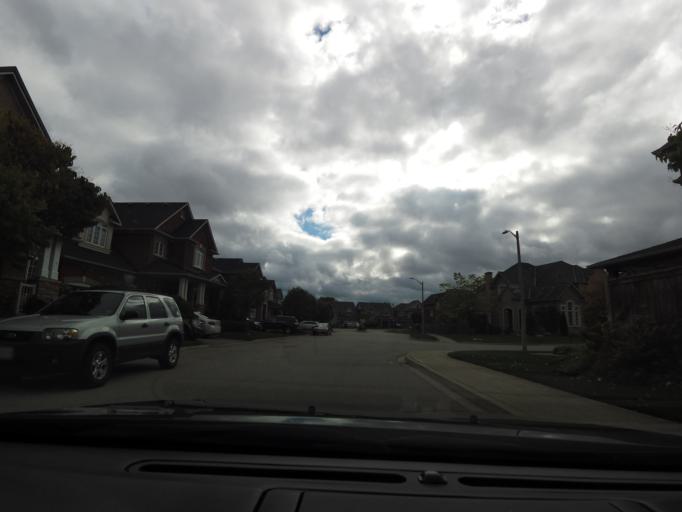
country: CA
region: Ontario
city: Burlington
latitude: 43.4042
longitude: -79.7872
